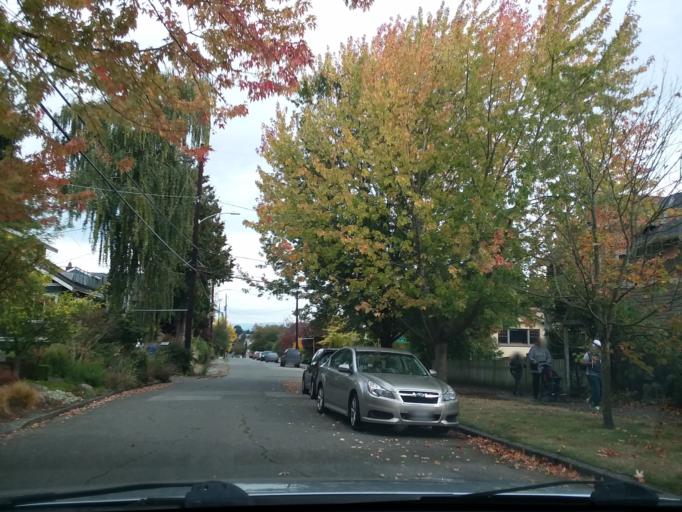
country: US
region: Washington
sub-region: King County
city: Seattle
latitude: 47.6578
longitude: -122.3531
